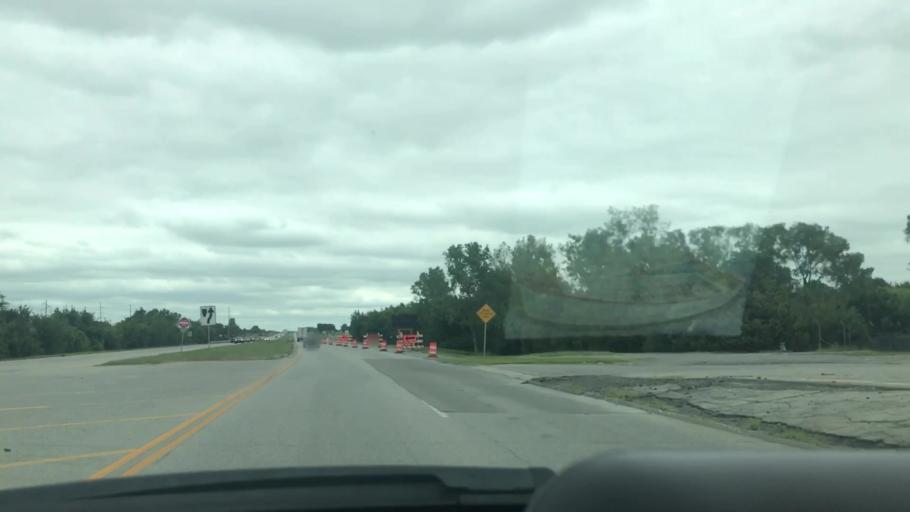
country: US
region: Oklahoma
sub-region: Mayes County
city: Pryor
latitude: 36.3179
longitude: -95.3150
